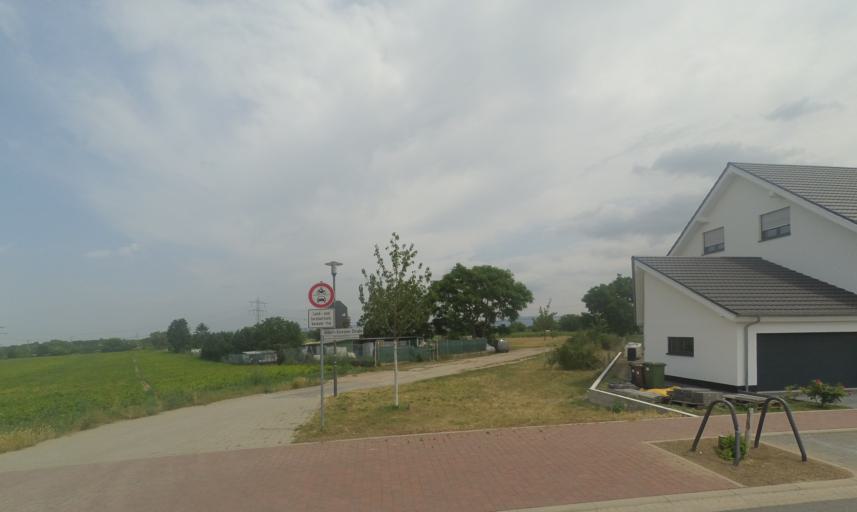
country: DE
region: Baden-Wuerttemberg
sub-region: Karlsruhe Region
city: Bruhl
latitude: 49.4016
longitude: 8.5393
